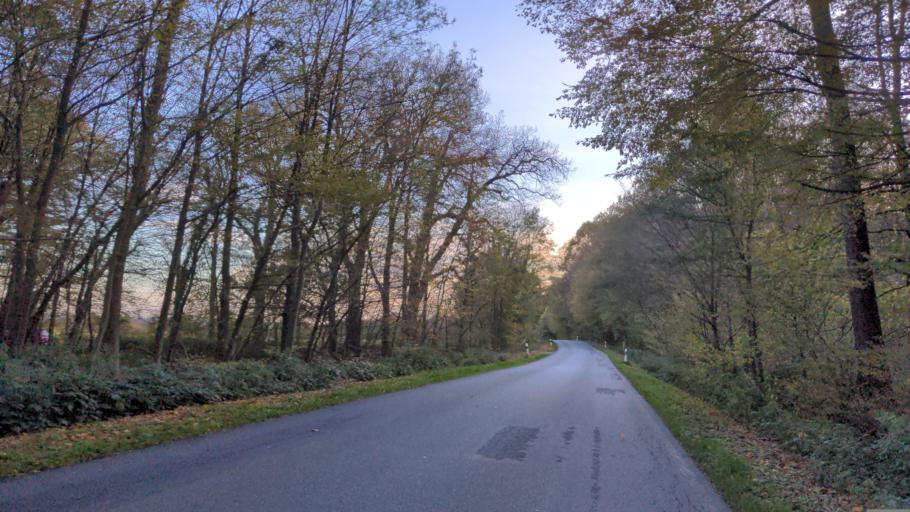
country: DE
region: Schleswig-Holstein
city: Reinfeld
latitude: 53.8489
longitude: 10.4718
